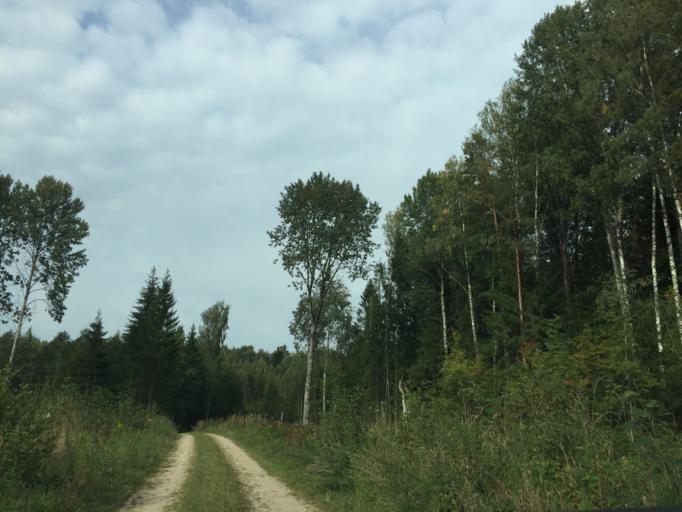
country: LV
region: Ikskile
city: Ikskile
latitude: 56.7584
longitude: 24.4749
